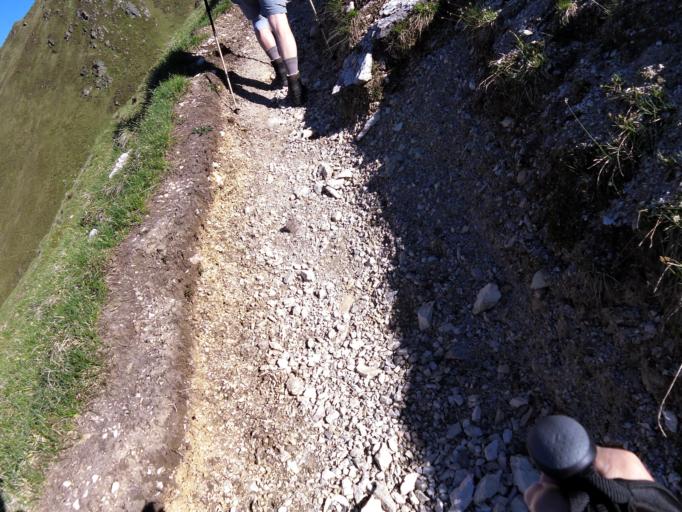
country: AT
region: Tyrol
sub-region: Politischer Bezirk Innsbruck Land
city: Neustift im Stubaital
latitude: 47.1286
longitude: 11.2794
